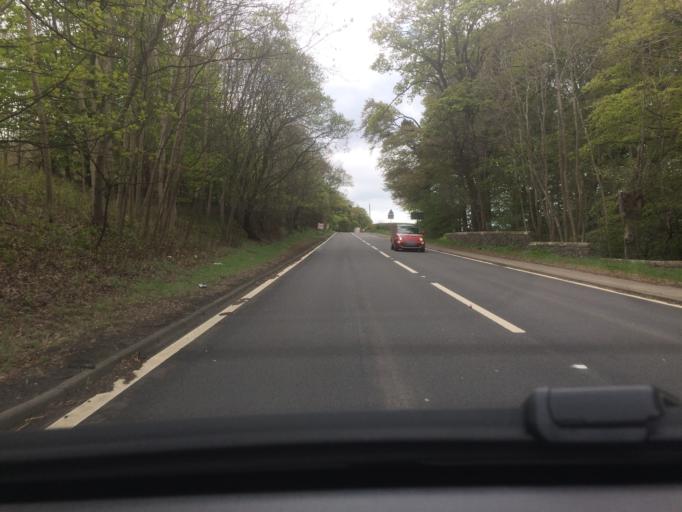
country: GB
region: Scotland
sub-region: Midlothian
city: Penicuik
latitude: 55.8541
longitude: -3.2246
